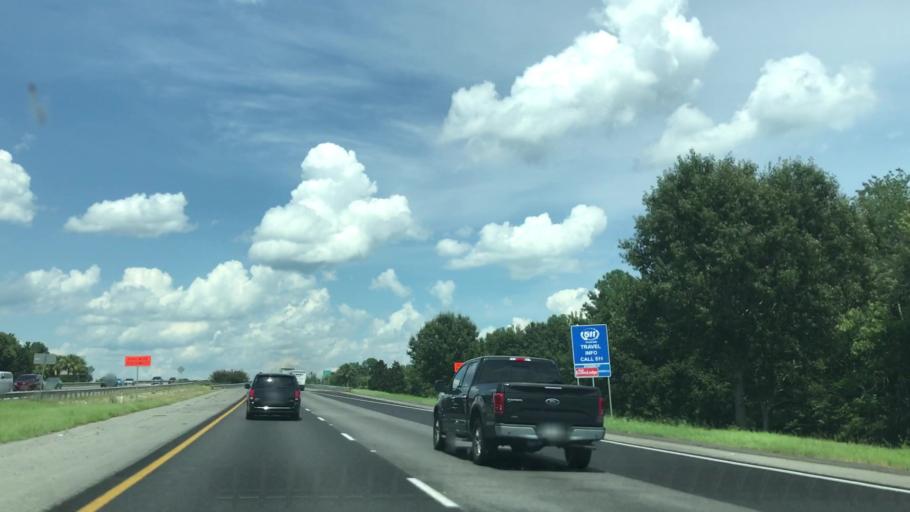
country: US
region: Georgia
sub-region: Chatham County
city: Port Wentworth
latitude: 32.2322
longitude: -81.1554
